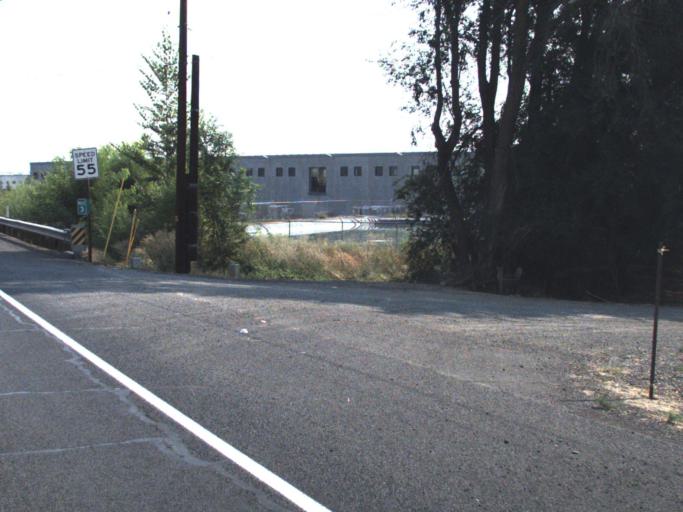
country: US
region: Washington
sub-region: Yakima County
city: Selah
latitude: 46.6721
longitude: -120.5152
